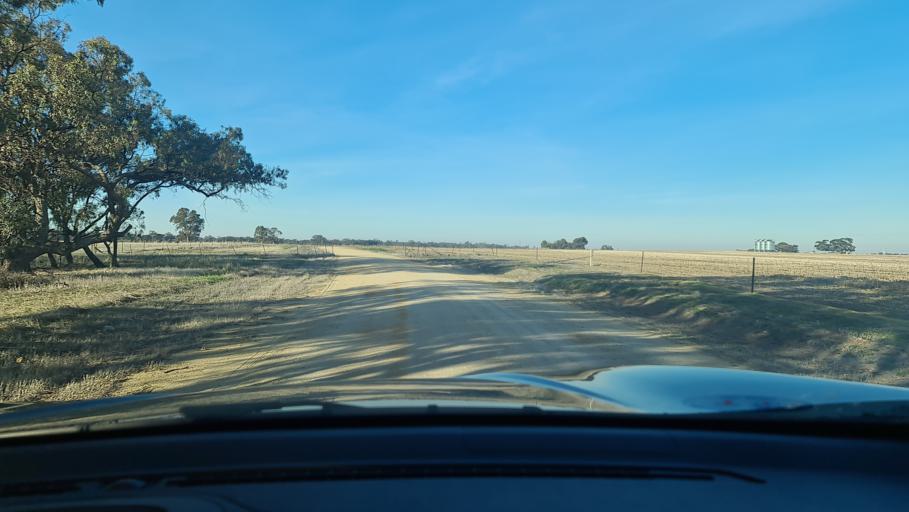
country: AU
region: Victoria
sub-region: Horsham
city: Horsham
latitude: -36.3595
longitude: 142.3963
